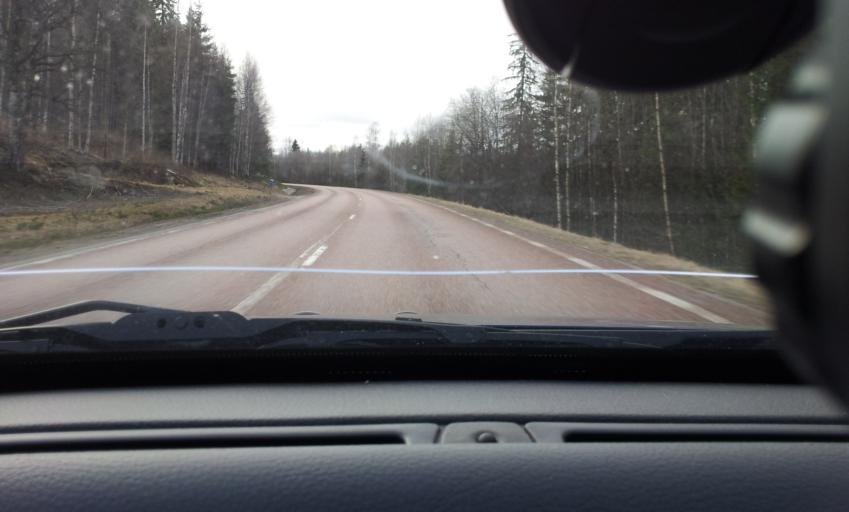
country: SE
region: Gaevleborg
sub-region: Ljusdals Kommun
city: Farila
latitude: 61.8847
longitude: 15.7050
